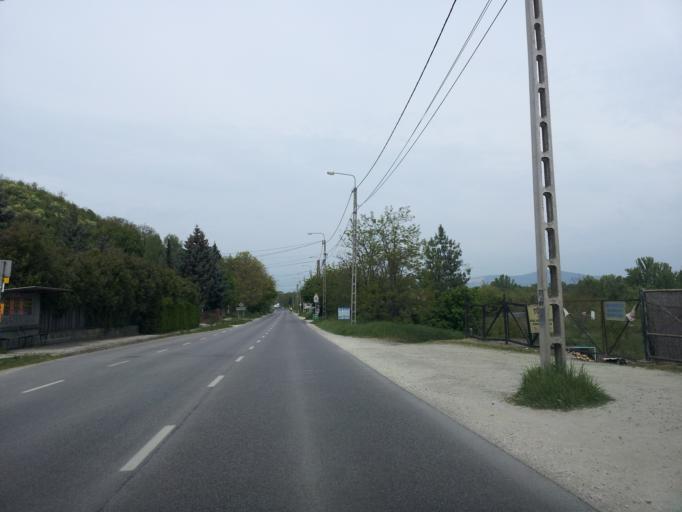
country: HU
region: Pest
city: Leanyfalu
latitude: 47.7308
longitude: 19.0886
